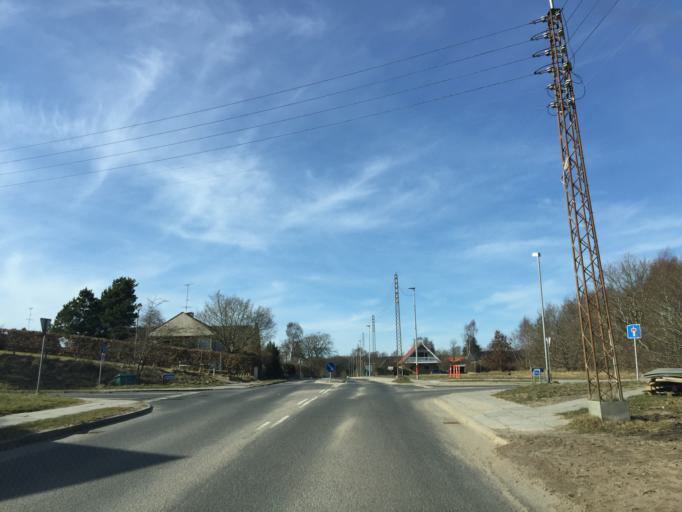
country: DK
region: Central Jutland
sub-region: Silkeborg Kommune
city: Silkeborg
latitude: 56.1930
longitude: 9.5366
